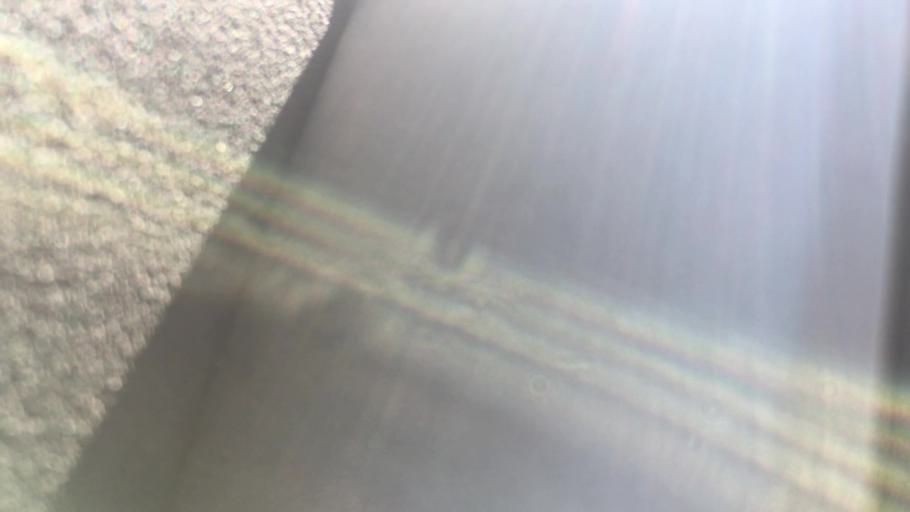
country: US
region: Maryland
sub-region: Worcester County
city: Pocomoke City
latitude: 38.0790
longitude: -75.5710
